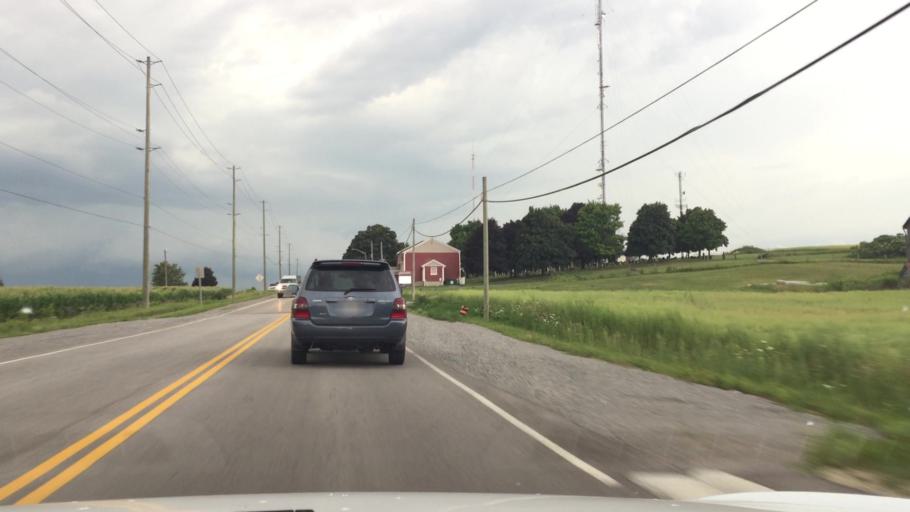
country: CA
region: Ontario
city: Oshawa
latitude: 43.9514
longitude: -78.8061
